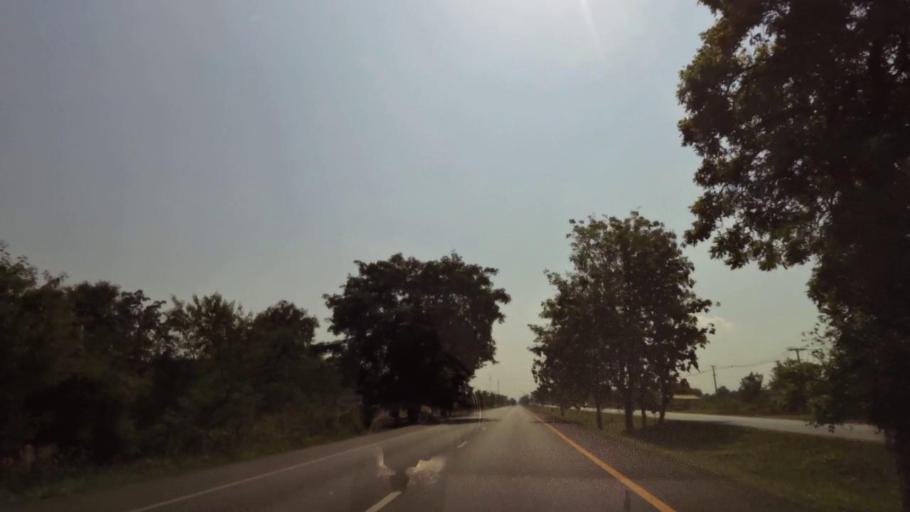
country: TH
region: Phichit
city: Bueng Na Rang
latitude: 16.2791
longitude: 100.1272
